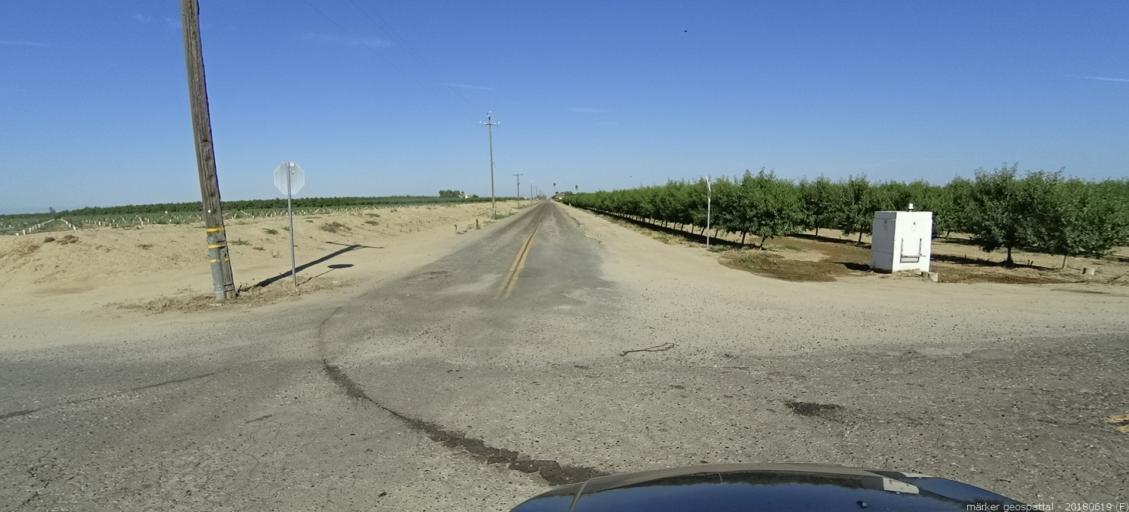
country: US
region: California
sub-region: Fresno County
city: Biola
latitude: 36.8296
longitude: -120.0247
